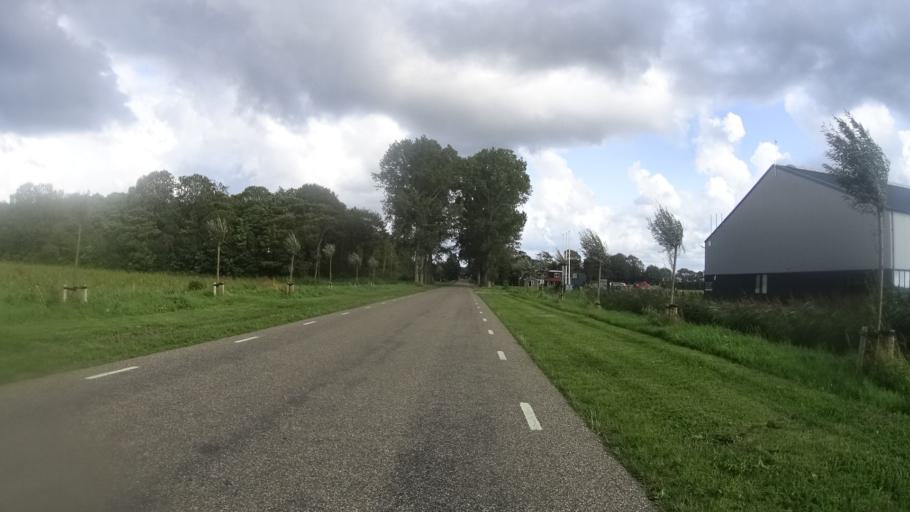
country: NL
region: North Holland
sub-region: Gemeente Hollands Kroon
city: Den Oever
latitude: 52.8994
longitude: 5.0108
